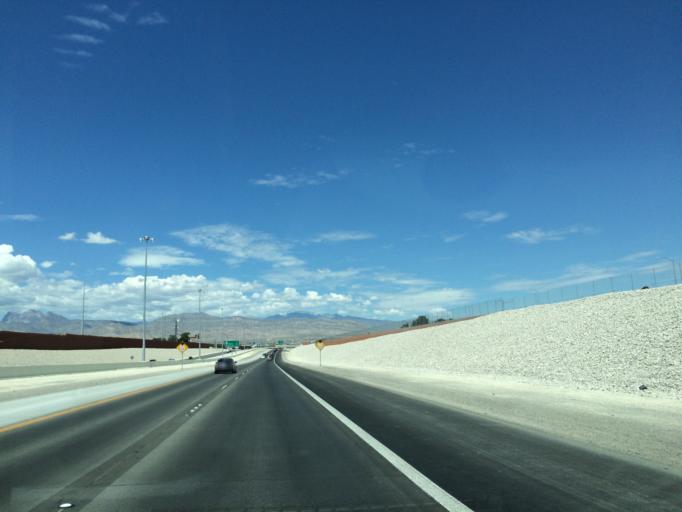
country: US
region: Nevada
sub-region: Clark County
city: Las Vegas
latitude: 36.2755
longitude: -115.2388
